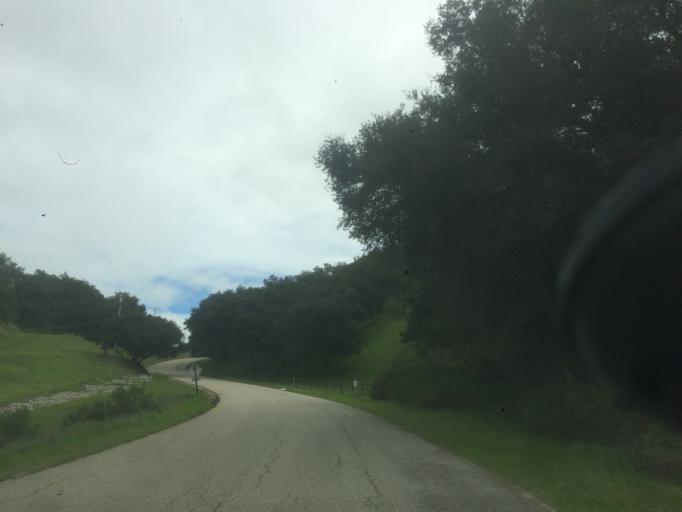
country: US
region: California
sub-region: San Luis Obispo County
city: Nipomo
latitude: 35.2060
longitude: -120.3743
